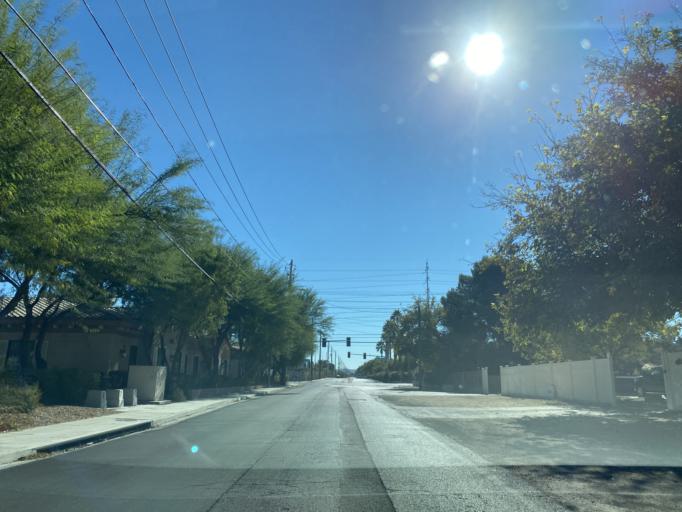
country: US
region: Nevada
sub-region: Clark County
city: Whitney
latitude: 36.0866
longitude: -115.0867
